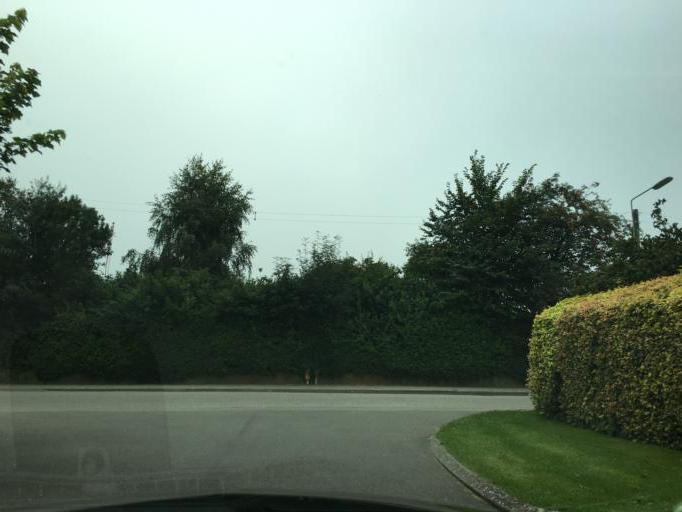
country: DK
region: South Denmark
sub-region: Kolding Kommune
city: Kolding
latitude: 55.5640
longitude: 9.4846
